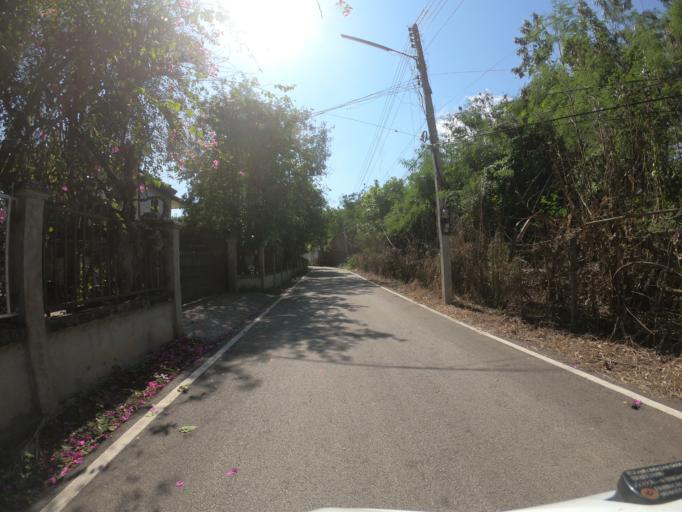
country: TH
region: Chiang Mai
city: Chiang Mai
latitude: 18.7468
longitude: 98.9676
